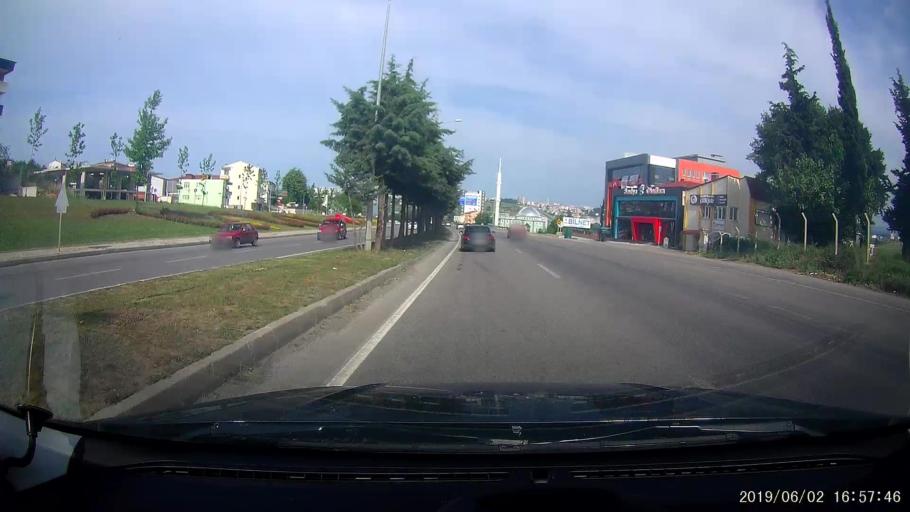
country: TR
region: Samsun
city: Samsun
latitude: 41.2903
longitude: 36.2781
